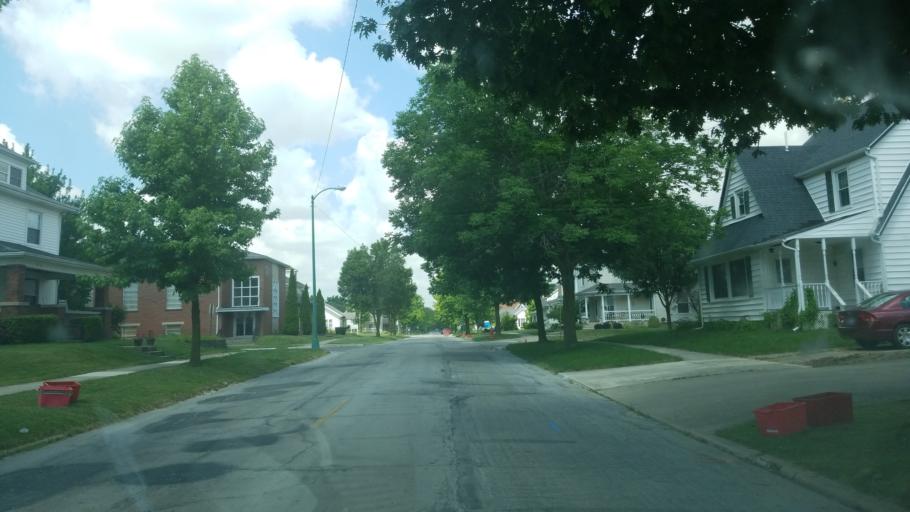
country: US
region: Ohio
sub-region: Auglaize County
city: Wapakoneta
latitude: 40.5670
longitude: -84.1986
